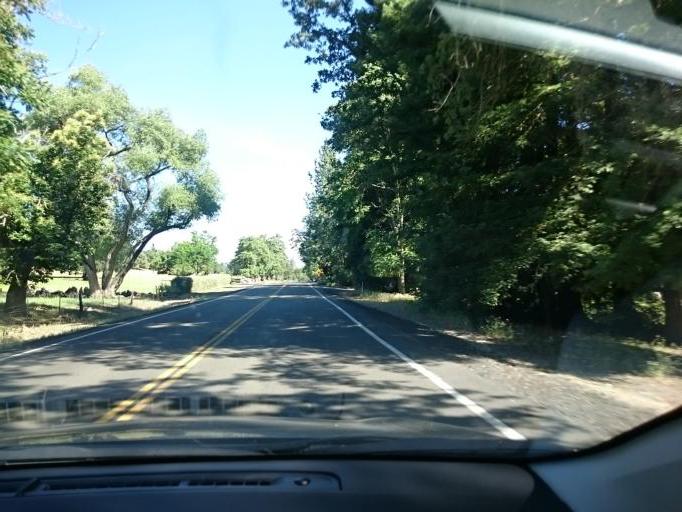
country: US
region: California
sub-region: Tuolumne County
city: Columbia
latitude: 38.0484
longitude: -120.4119
